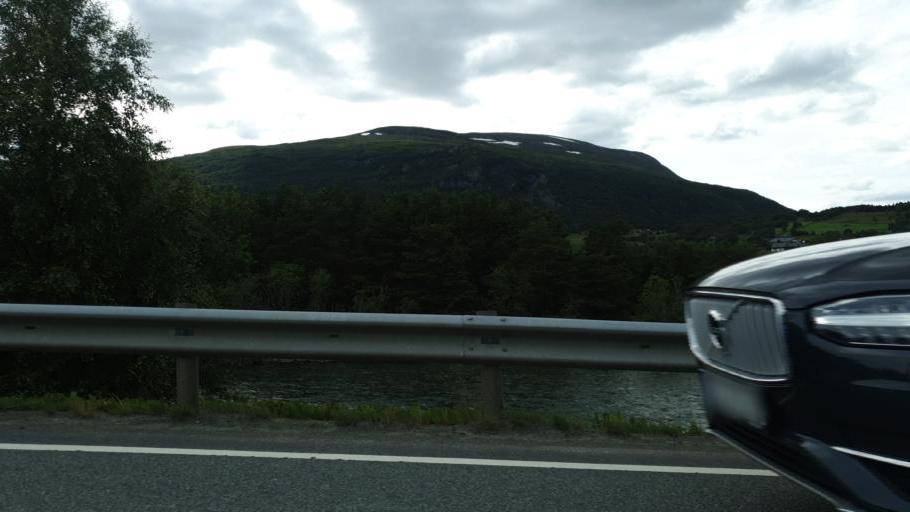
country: NO
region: Sor-Trondelag
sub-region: Oppdal
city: Oppdal
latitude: 62.5519
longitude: 9.6325
